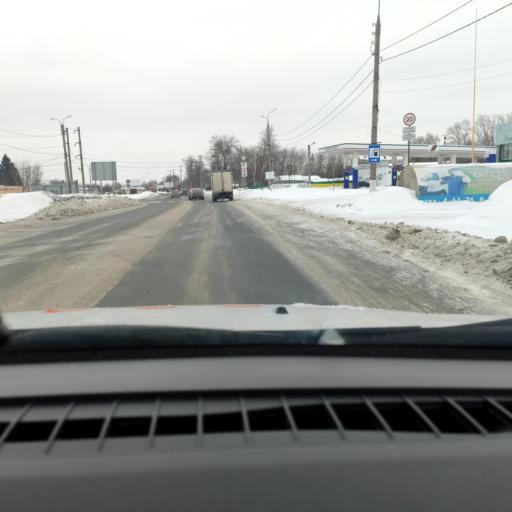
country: RU
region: Samara
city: Novokuybyshevsk
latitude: 53.1170
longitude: 49.9350
